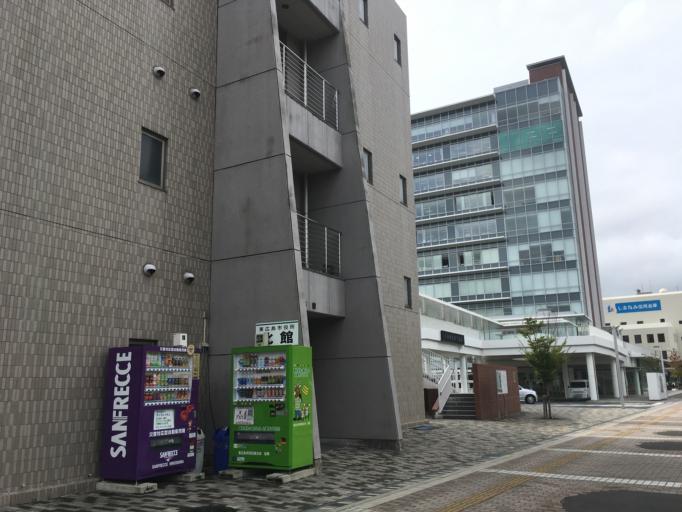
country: JP
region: Hiroshima
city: Takehara
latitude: 34.4273
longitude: 132.7431
